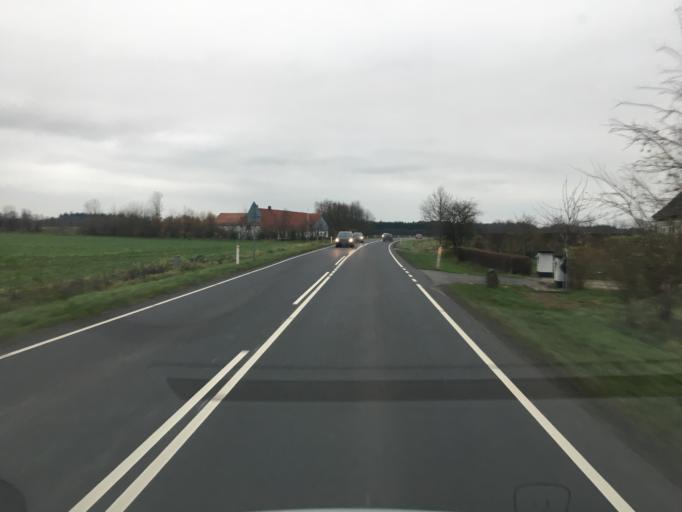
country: DK
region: South Denmark
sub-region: Aabenraa Kommune
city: Tinglev
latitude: 54.9753
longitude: 9.1361
